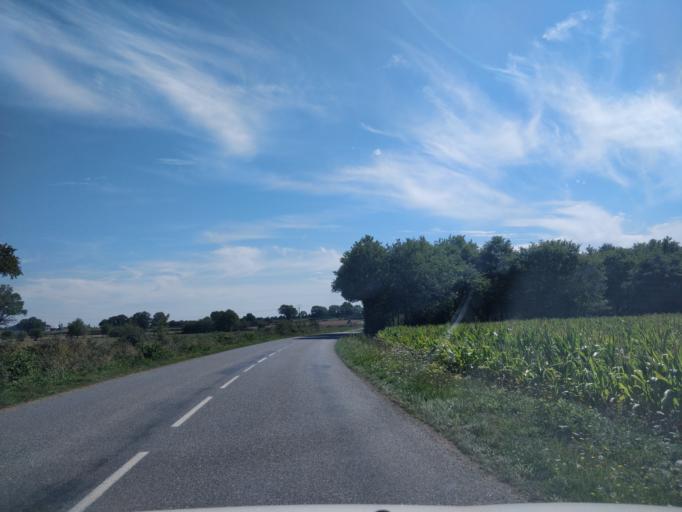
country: FR
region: Pays de la Loire
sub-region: Departement de la Loire-Atlantique
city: Derval
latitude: 47.6886
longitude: -1.6962
